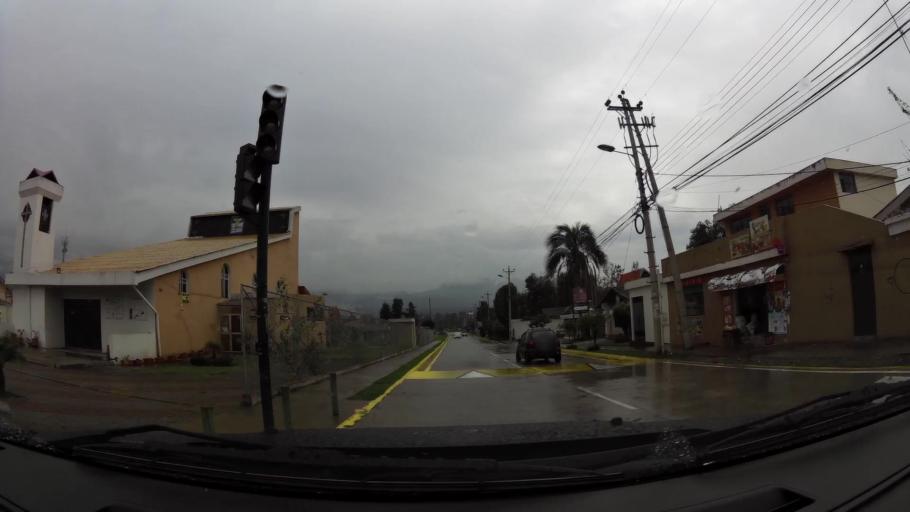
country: EC
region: Pichincha
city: Sangolqui
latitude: -0.2920
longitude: -78.4566
